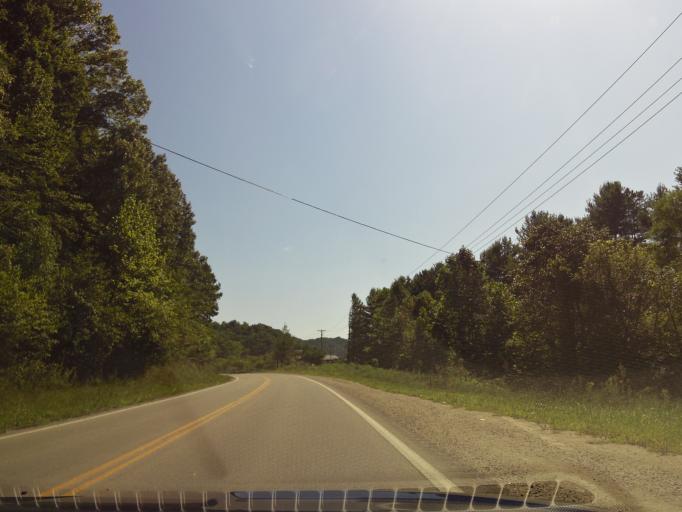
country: US
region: Kentucky
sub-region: Clay County
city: Manchester
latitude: 37.1207
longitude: -83.7442
